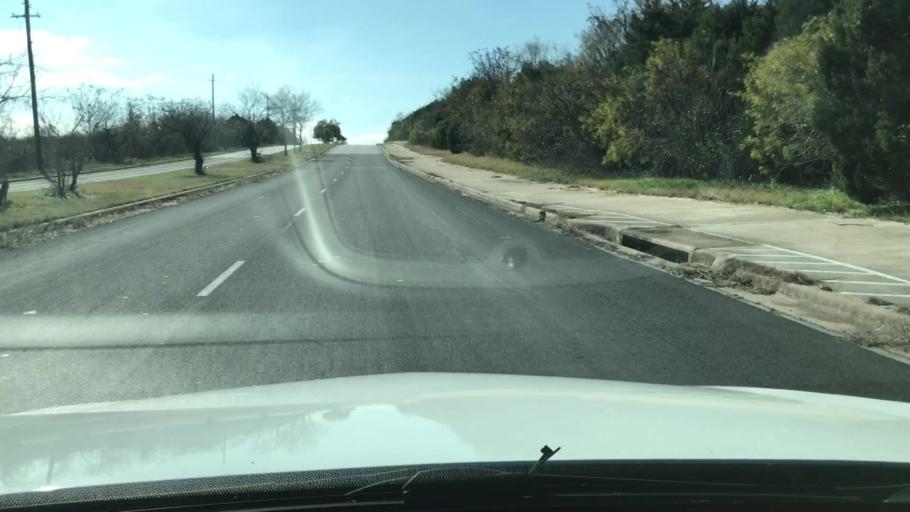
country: US
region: Texas
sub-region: Travis County
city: Onion Creek
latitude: 30.1767
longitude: -97.7216
